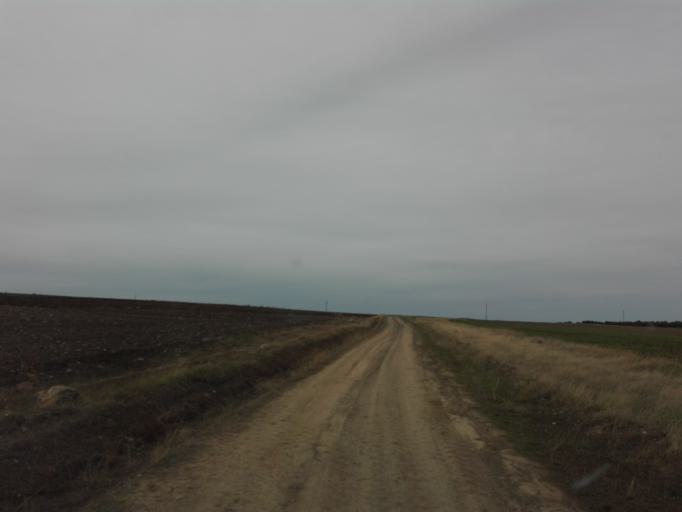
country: ES
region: Extremadura
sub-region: Provincia de Badajoz
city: Llerena
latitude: 38.2553
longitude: -6.0142
